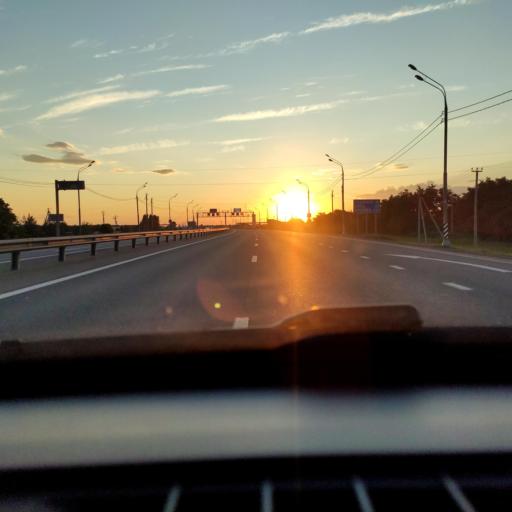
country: RU
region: Lipetsk
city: Khlevnoye
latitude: 52.2171
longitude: 39.1400
